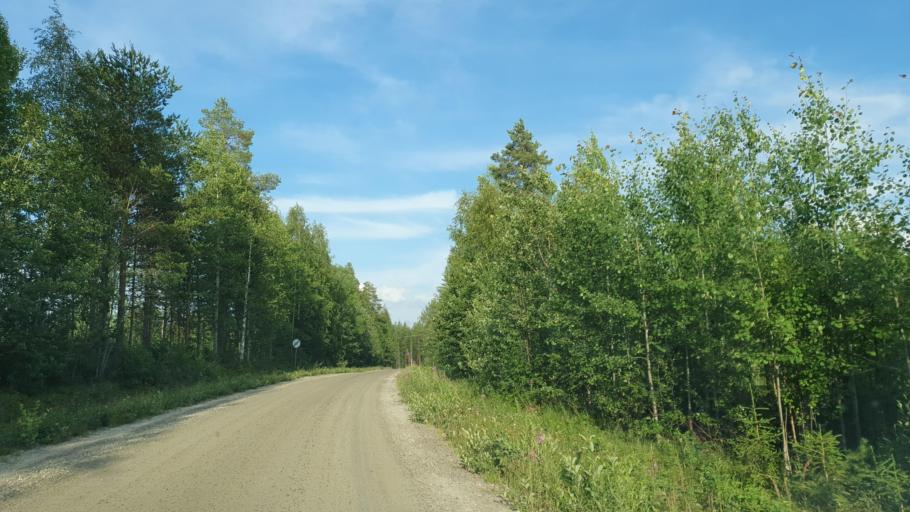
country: FI
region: Kainuu
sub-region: Kehys-Kainuu
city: Kuhmo
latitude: 64.2669
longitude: 29.8156
